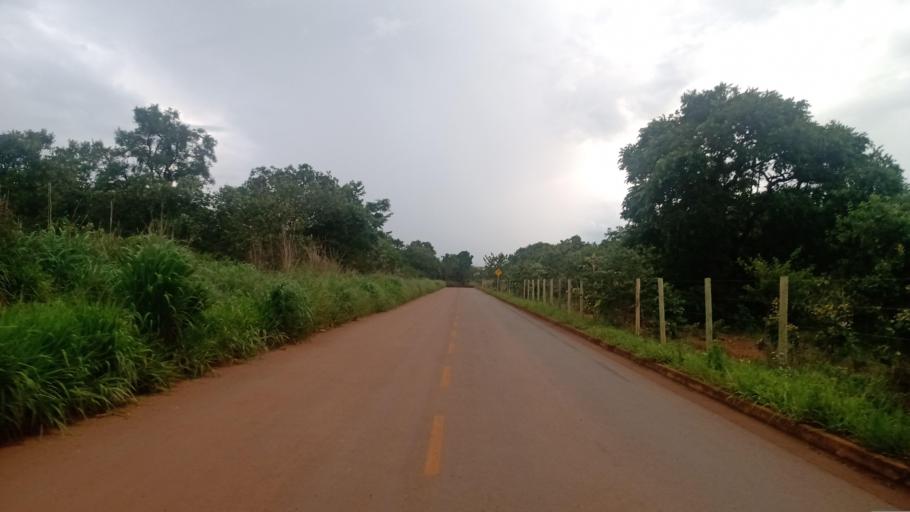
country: BR
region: Goias
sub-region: Senador Canedo
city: Senador Canedo
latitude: -16.7121
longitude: -49.1177
